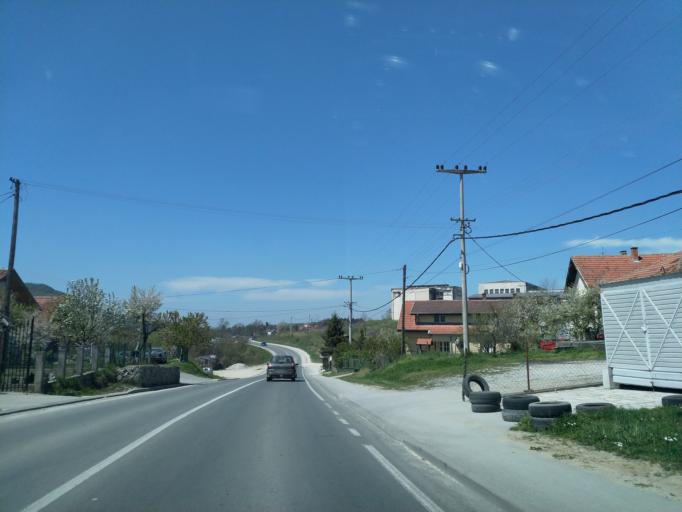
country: RS
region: Central Serbia
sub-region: Sumadijski Okrug
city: Arangelovac
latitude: 44.3254
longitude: 20.5283
